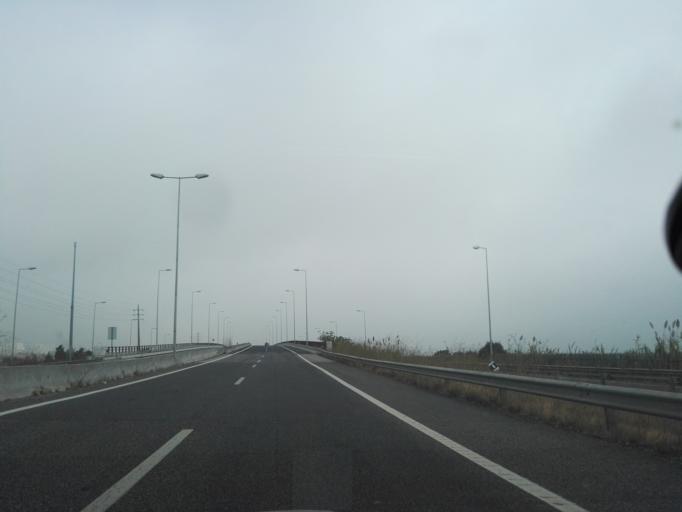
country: PT
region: Lisbon
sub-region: Loures
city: Santa Iria da Azoia
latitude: 38.8327
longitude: -9.0777
